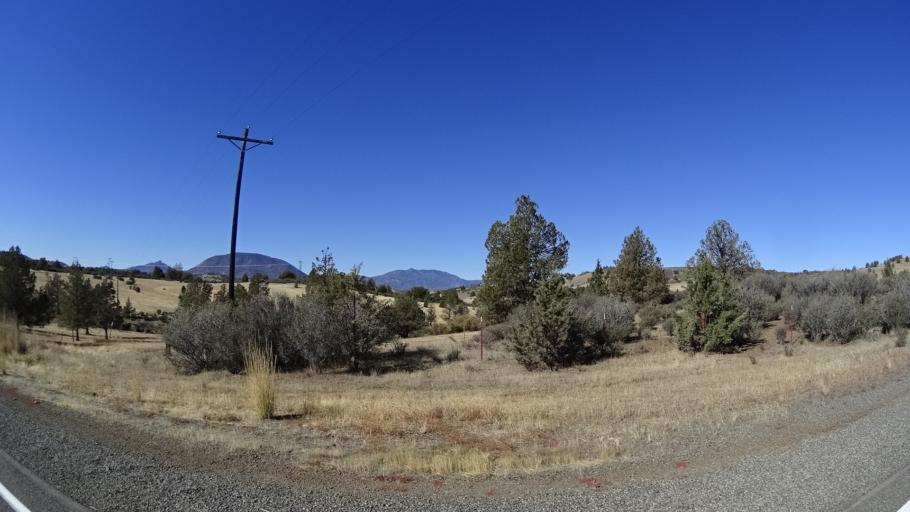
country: US
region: California
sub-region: Siskiyou County
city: Montague
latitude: 41.8962
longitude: -122.3976
